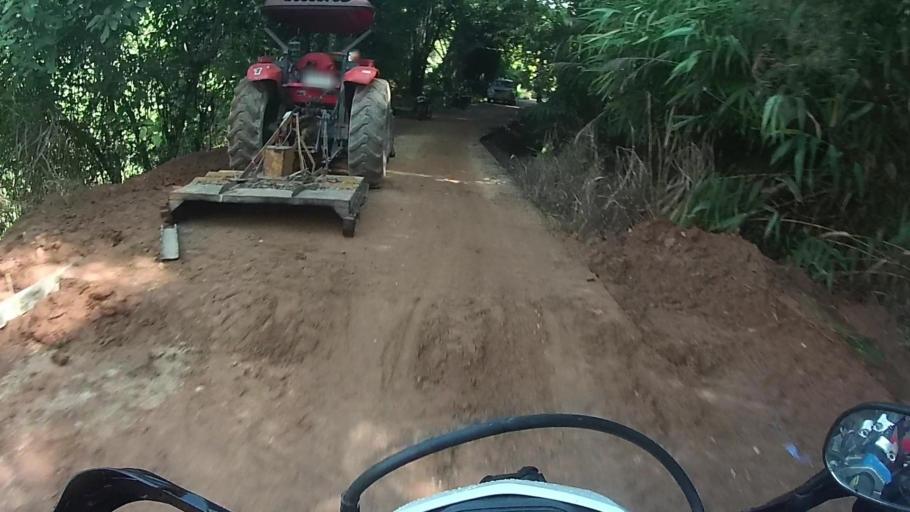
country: TH
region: Chiang Mai
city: Mae Taeng
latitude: 19.0035
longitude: 98.8659
